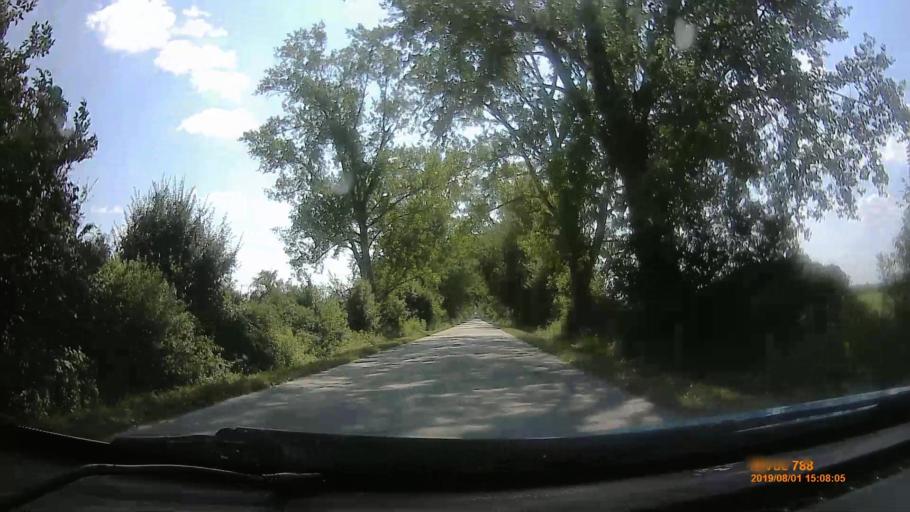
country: HU
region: Baranya
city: Sellye
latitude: 45.8540
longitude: 17.8224
